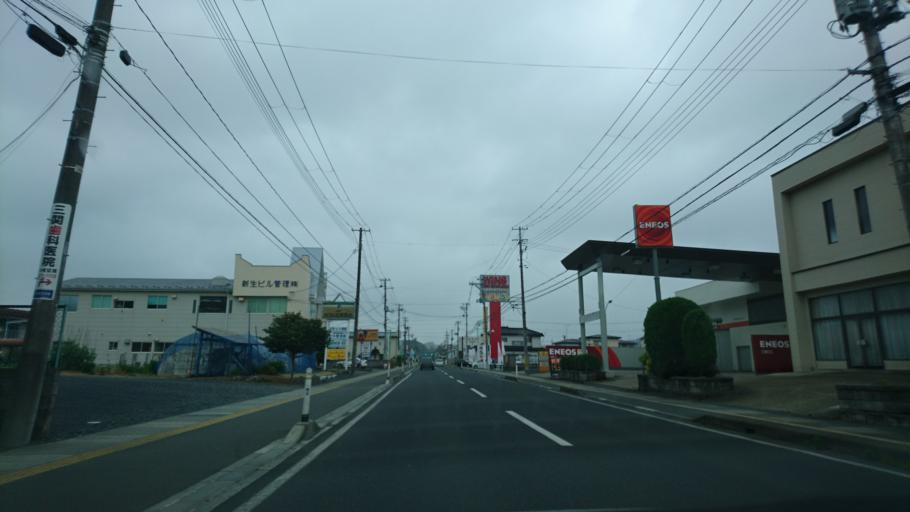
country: JP
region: Iwate
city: Ichinoseki
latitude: 38.9275
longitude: 141.1500
